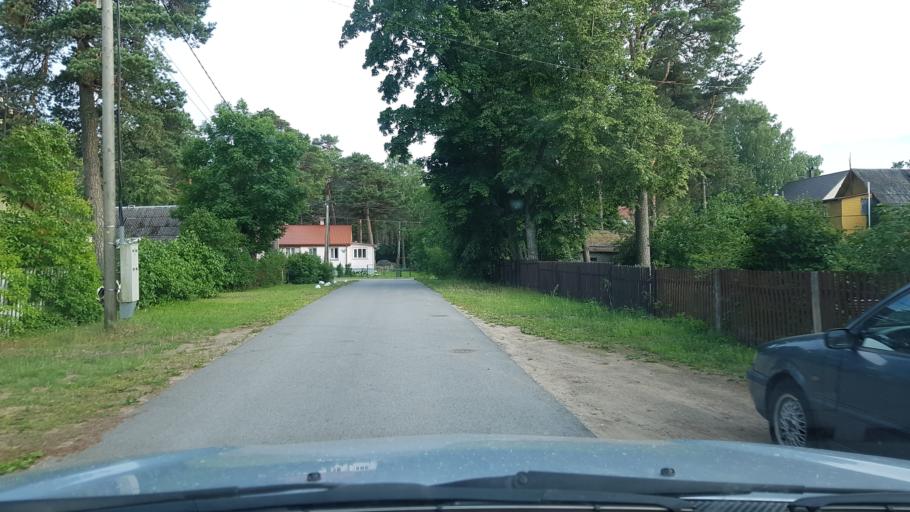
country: EE
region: Ida-Virumaa
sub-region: Narva-Joesuu linn
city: Narva-Joesuu
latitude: 59.4570
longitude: 28.0517
